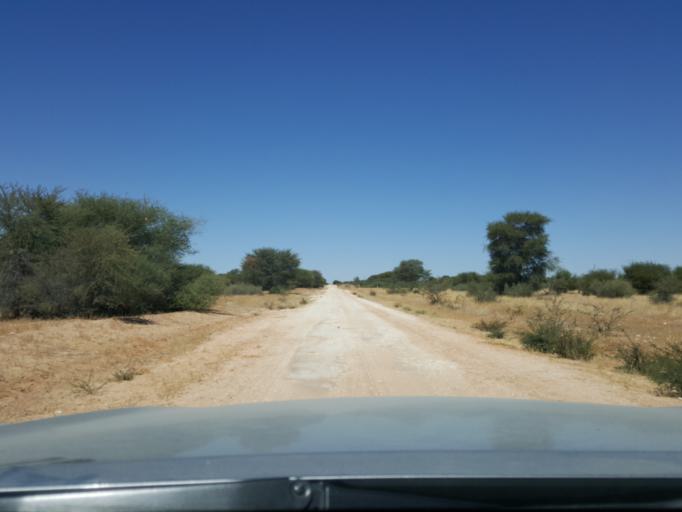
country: BW
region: Kgalagadi
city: Hukuntsi
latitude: -23.9944
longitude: 21.2109
